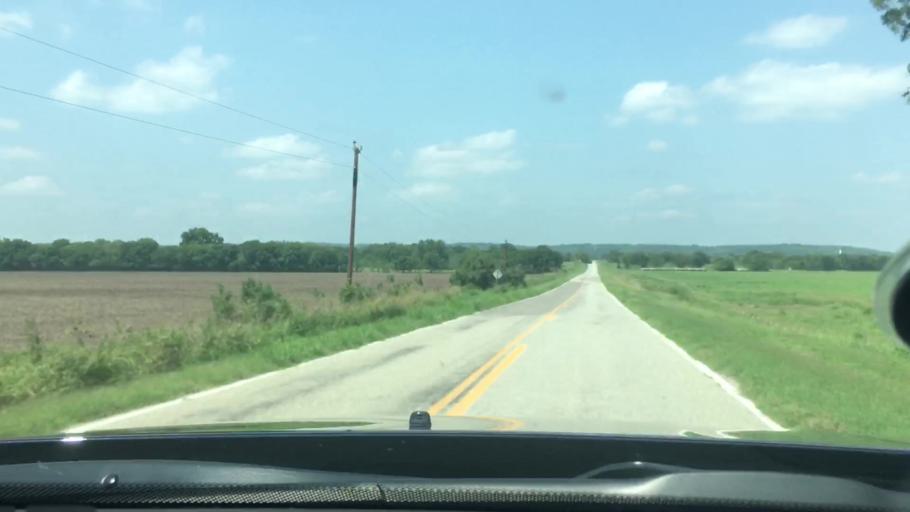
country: US
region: Oklahoma
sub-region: Johnston County
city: Tishomingo
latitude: 34.3904
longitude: -96.4962
